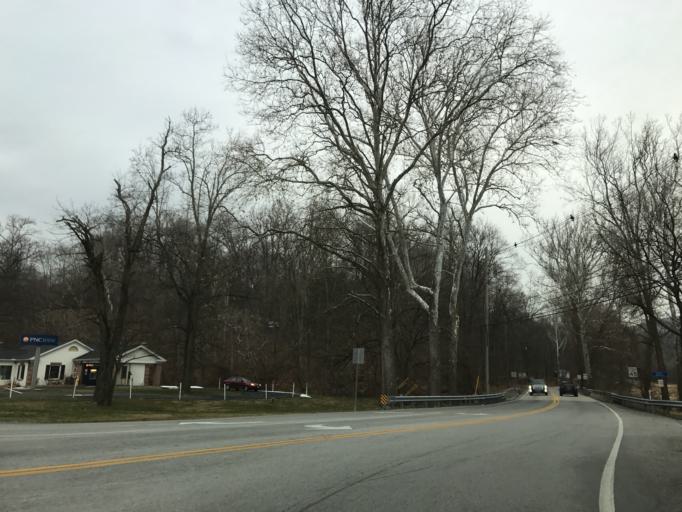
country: US
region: Pennsylvania
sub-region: Adams County
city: Carroll Valley
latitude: 39.7350
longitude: -77.3711
